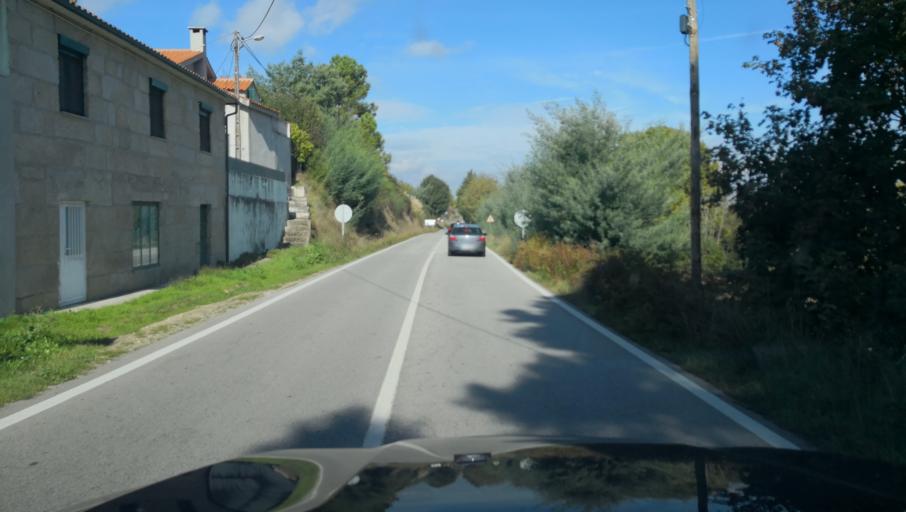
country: PT
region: Vila Real
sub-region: Chaves
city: Chaves
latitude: 41.7262
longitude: -7.4789
